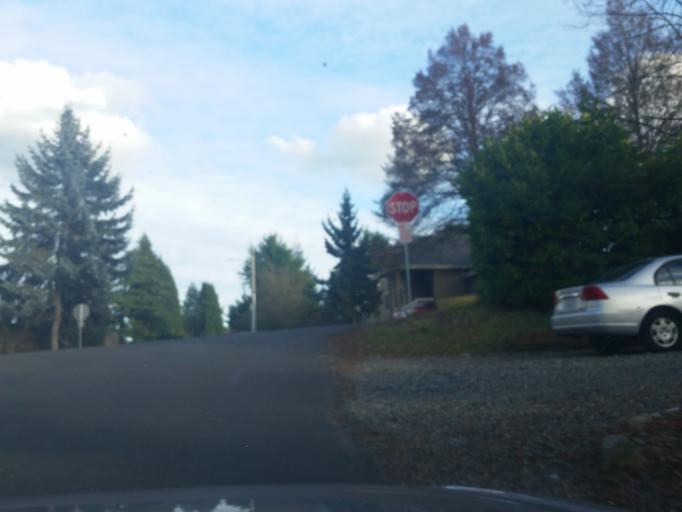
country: US
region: Washington
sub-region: King County
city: Shoreline
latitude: 47.7050
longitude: -122.3182
